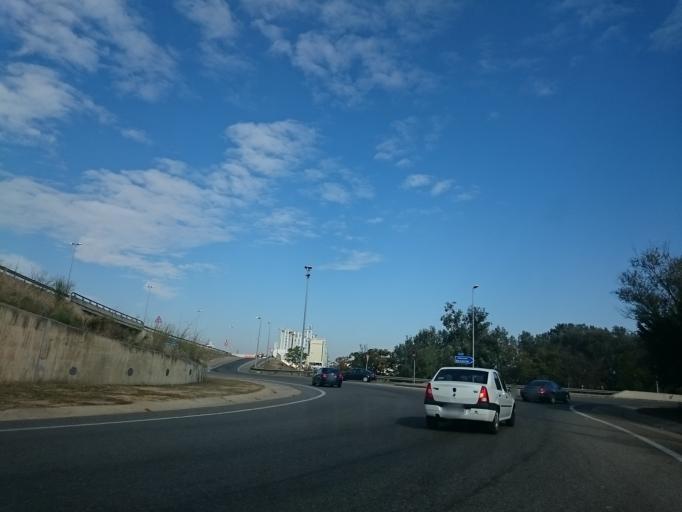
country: ES
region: Catalonia
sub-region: Provincia de Lleida
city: Alcoletge
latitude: 41.6180
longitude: 0.6653
